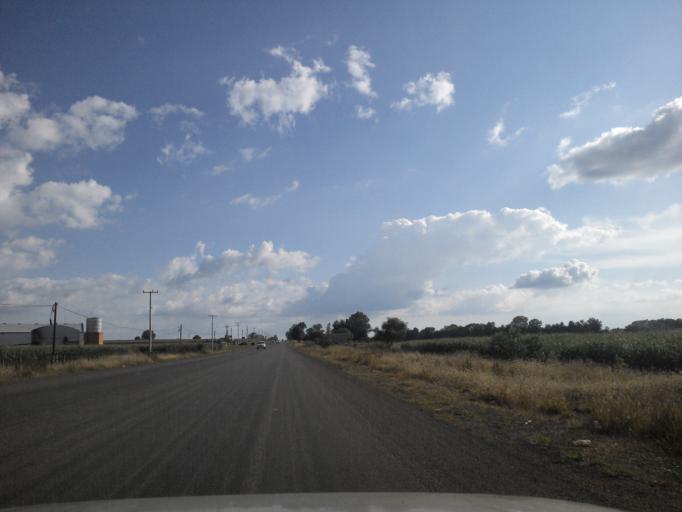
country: MX
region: Jalisco
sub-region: Atotonilco el Alto
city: Ojo de Agua de Moran
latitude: 20.5957
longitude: -102.4942
